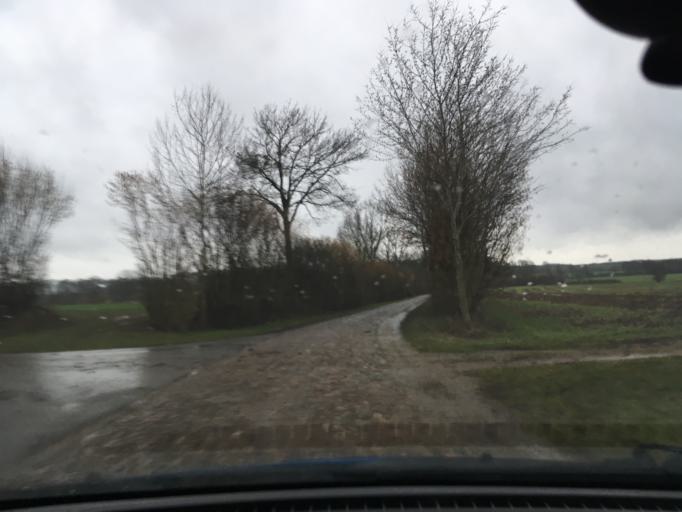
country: DE
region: Schleswig-Holstein
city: Kruzen
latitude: 53.4077
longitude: 10.5212
